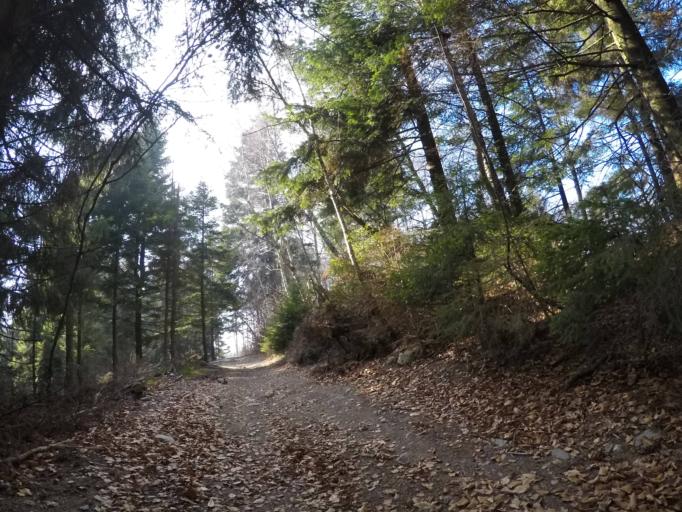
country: SK
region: Kosicky
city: Gelnica
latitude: 48.7638
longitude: 21.0551
